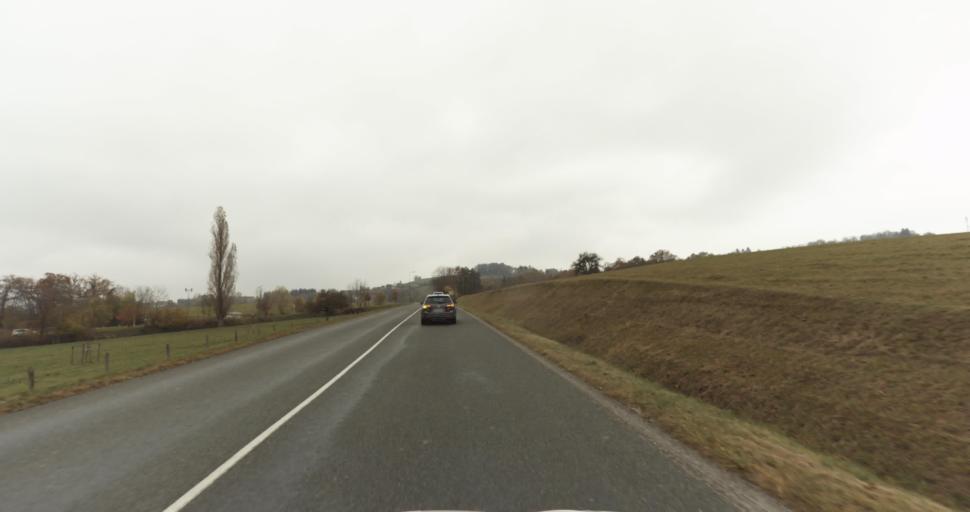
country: FR
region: Rhone-Alpes
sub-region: Departement de la Haute-Savoie
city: Alby-sur-Cheran
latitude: 45.8070
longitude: 6.0121
